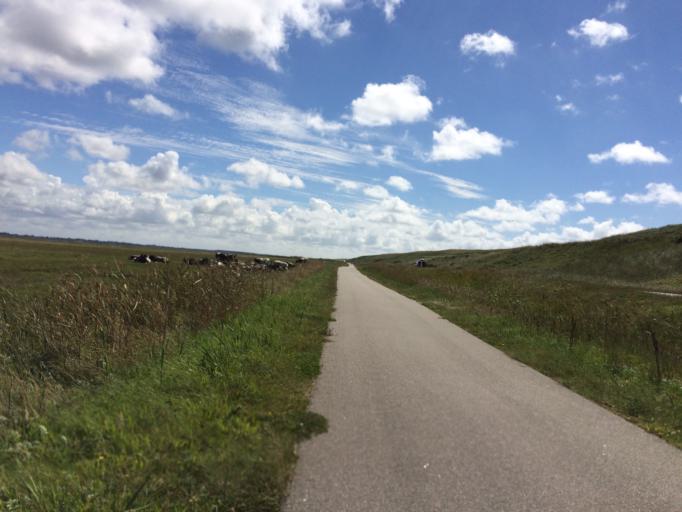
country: DK
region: Central Jutland
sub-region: Holstebro Kommune
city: Ulfborg
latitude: 56.3609
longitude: 8.1226
